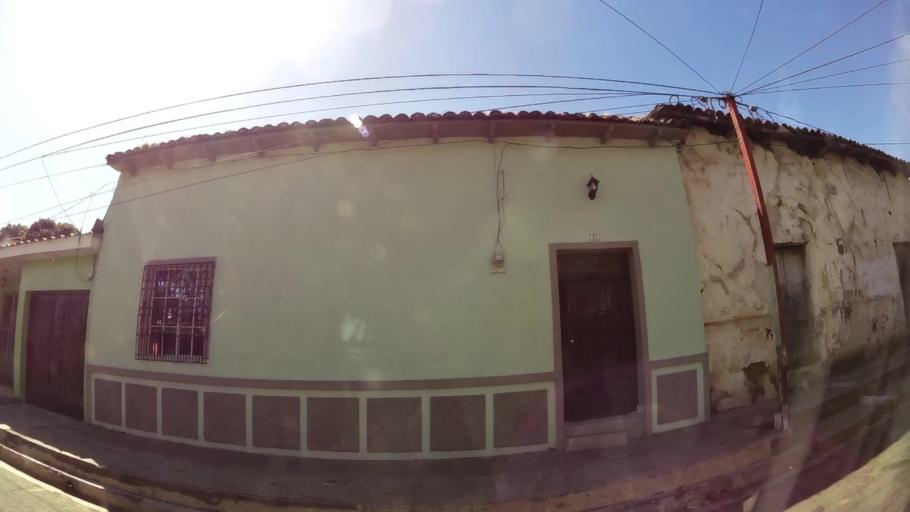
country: SV
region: Ahuachapan
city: Ahuachapan
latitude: 13.9194
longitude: -89.8511
